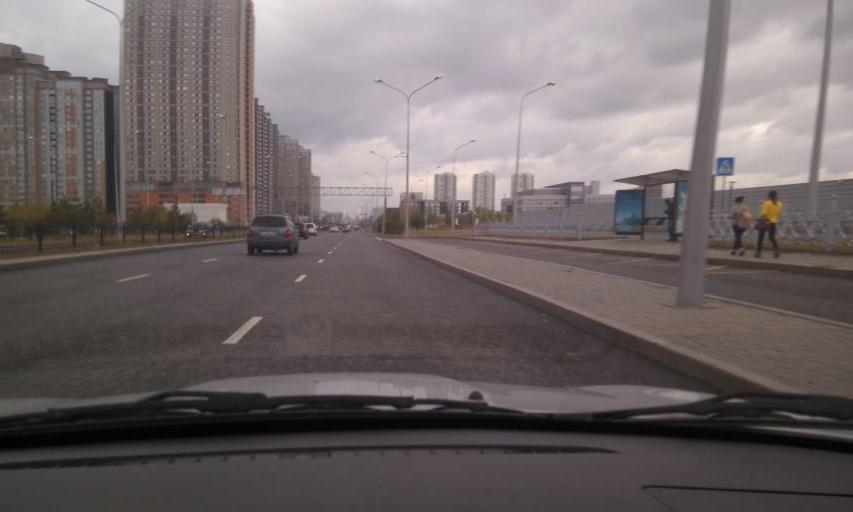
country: KZ
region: Astana Qalasy
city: Astana
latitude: 51.1269
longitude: 71.4752
